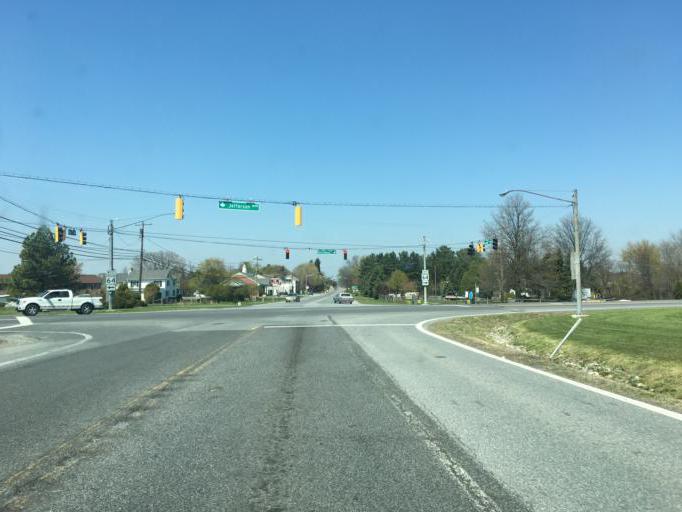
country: US
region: Maryland
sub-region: Washington County
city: Smithsburg
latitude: 39.6486
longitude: -77.5679
